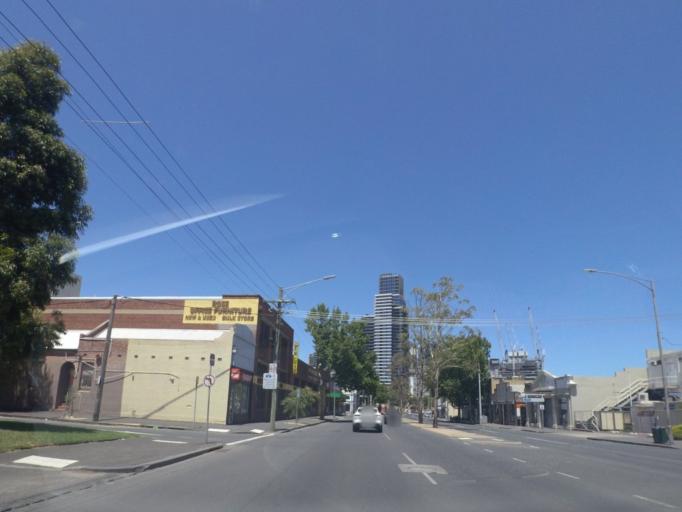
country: AU
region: Victoria
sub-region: Melbourne
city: West Melbourne
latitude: -37.8077
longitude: 144.9480
